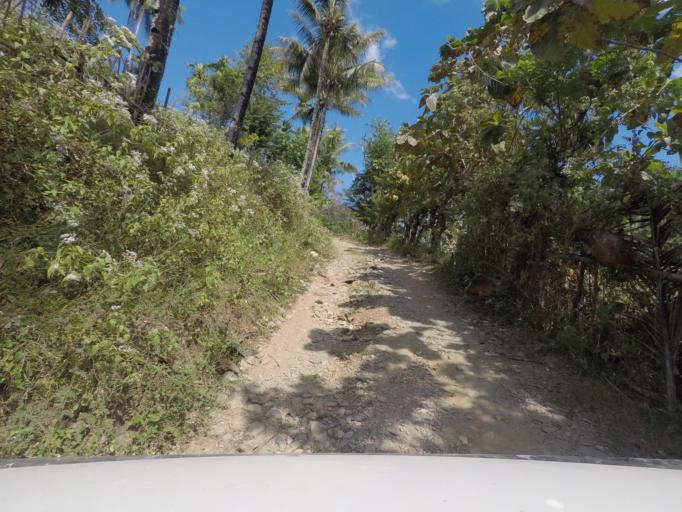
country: TL
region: Ermera
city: Gleno
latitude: -8.7189
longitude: 125.3068
